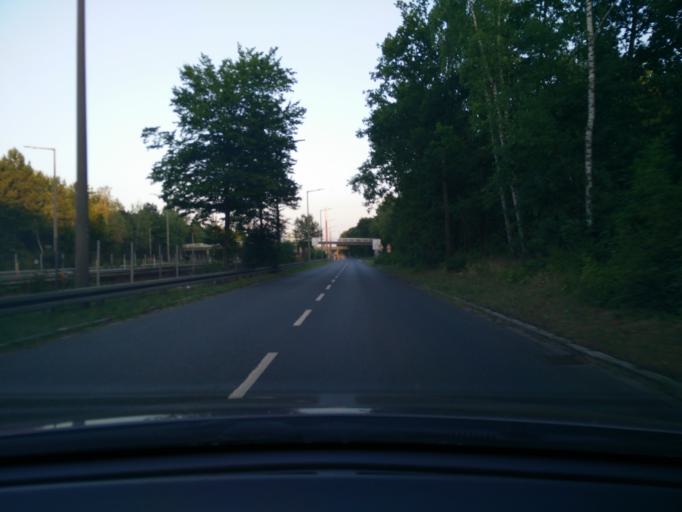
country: DE
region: Bavaria
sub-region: Regierungsbezirk Mittelfranken
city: Nuernberg
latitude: 49.4141
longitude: 11.1192
